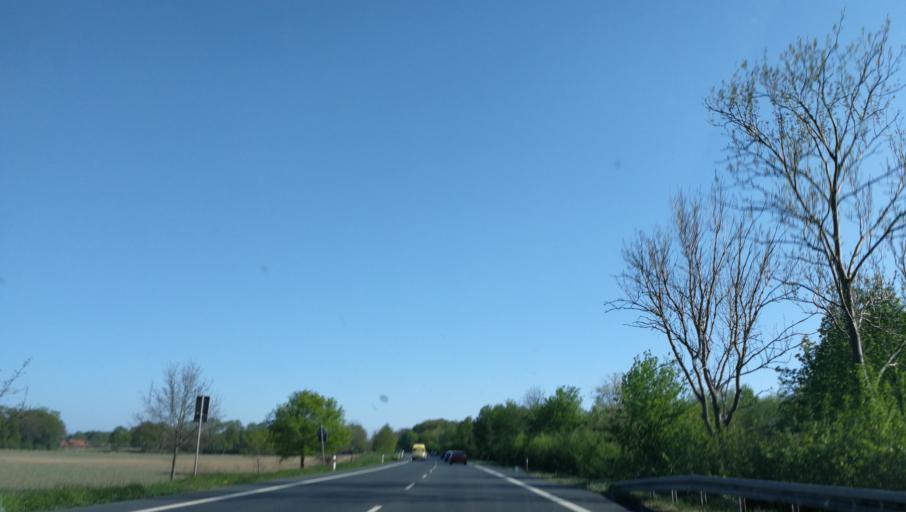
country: DE
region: North Rhine-Westphalia
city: Emsdetten
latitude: 52.1944
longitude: 7.5183
